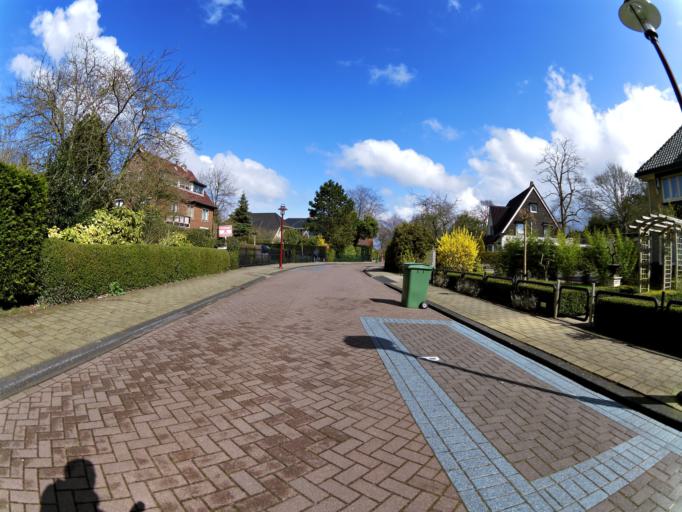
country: NL
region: South Holland
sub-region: Gemeente Hellevoetsluis
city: Nieuw-Helvoet
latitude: 51.8728
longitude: 4.0580
